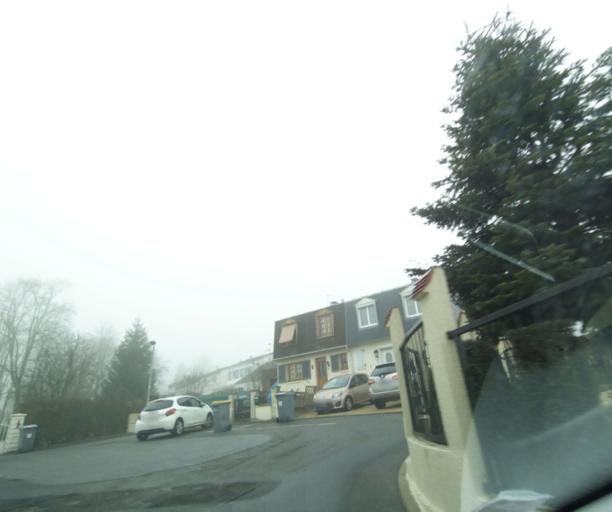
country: FR
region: Ile-de-France
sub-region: Departement de Seine-et-Marne
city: Dammartin-en-Goele
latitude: 49.0559
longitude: 2.6954
